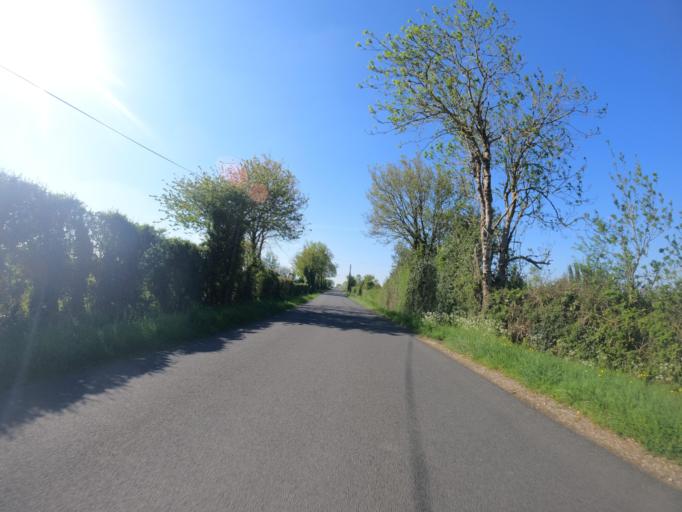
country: FR
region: Poitou-Charentes
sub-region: Departement des Deux-Sevres
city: La Chapelle-Saint-Laurent
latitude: 46.6978
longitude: -0.5177
